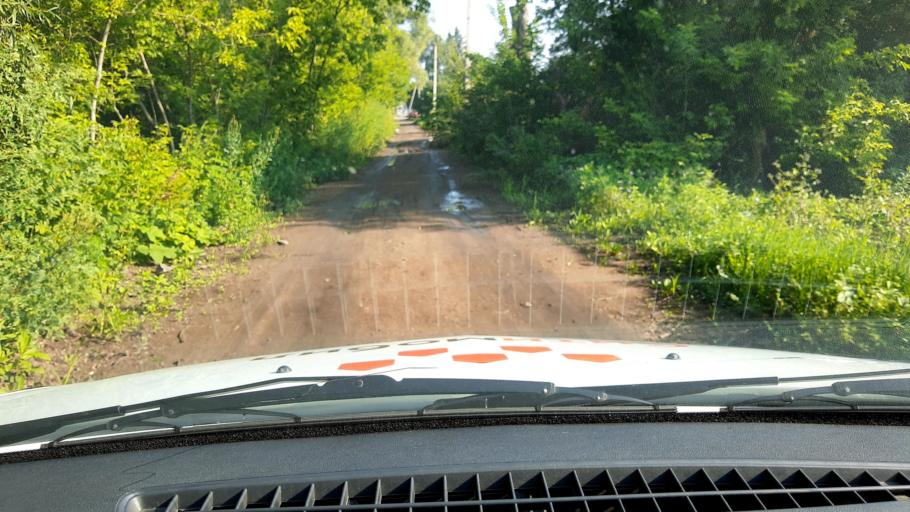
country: RU
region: Bashkortostan
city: Mikhaylovka
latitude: 54.6906
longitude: 55.8495
